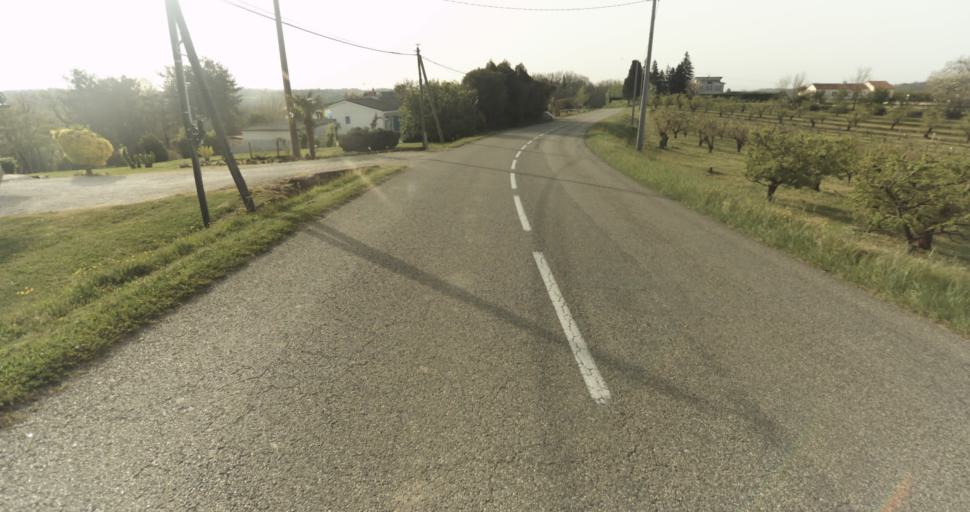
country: FR
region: Midi-Pyrenees
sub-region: Departement du Tarn-et-Garonne
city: Moissac
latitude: 44.1541
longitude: 1.0980
